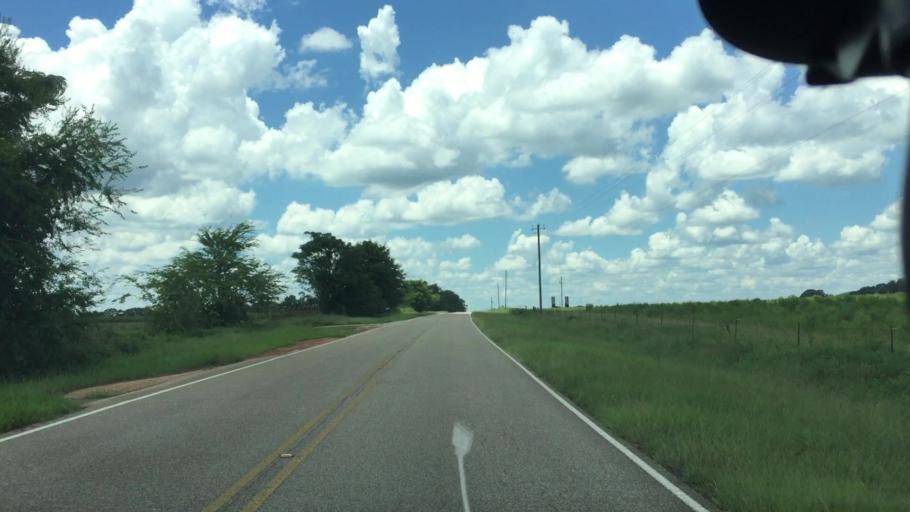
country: US
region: Alabama
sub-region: Coffee County
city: New Brockton
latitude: 31.4145
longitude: -85.8701
